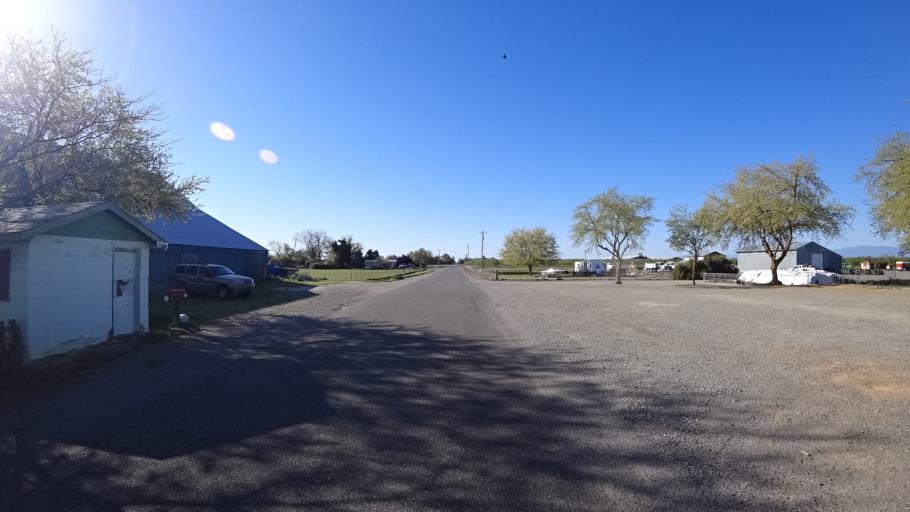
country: US
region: California
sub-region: Glenn County
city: Orland
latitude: 39.7528
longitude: -122.2389
